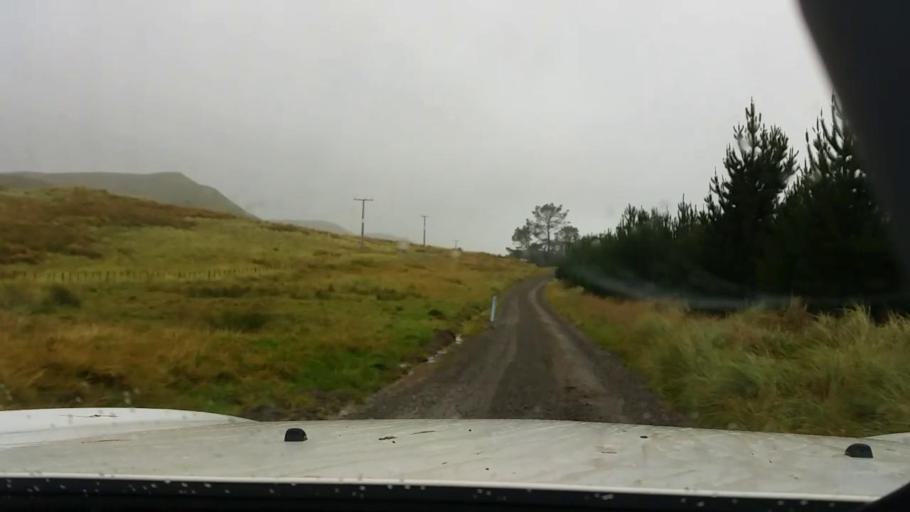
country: NZ
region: Wellington
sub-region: Masterton District
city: Masterton
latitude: -41.2530
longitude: 175.9134
